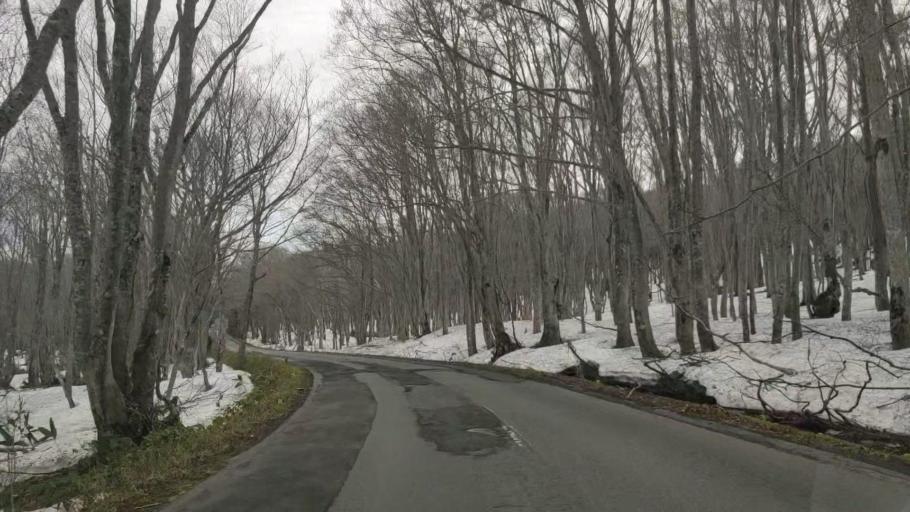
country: JP
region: Aomori
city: Aomori Shi
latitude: 40.6982
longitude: 140.9032
